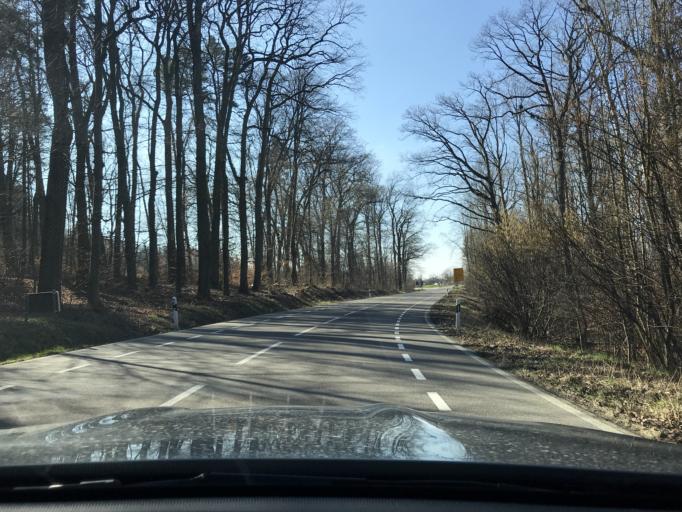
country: DE
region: Baden-Wuerttemberg
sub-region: Regierungsbezirk Stuttgart
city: Korb
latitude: 48.8624
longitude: 9.3673
